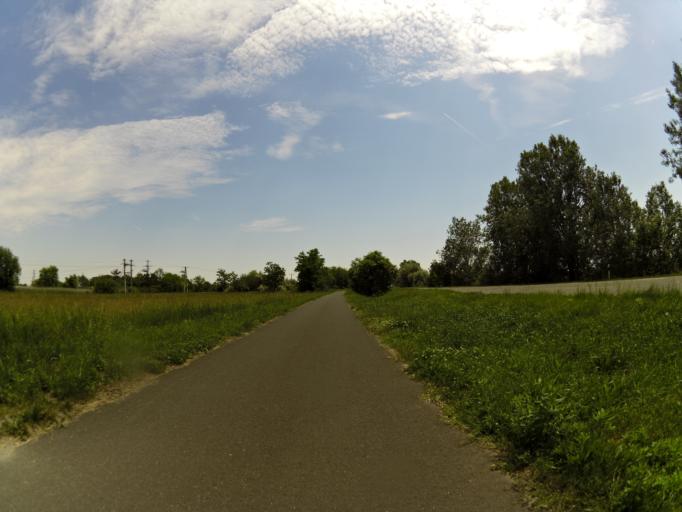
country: HU
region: Csongrad
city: Kistelek
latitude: 46.4587
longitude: 19.9902
